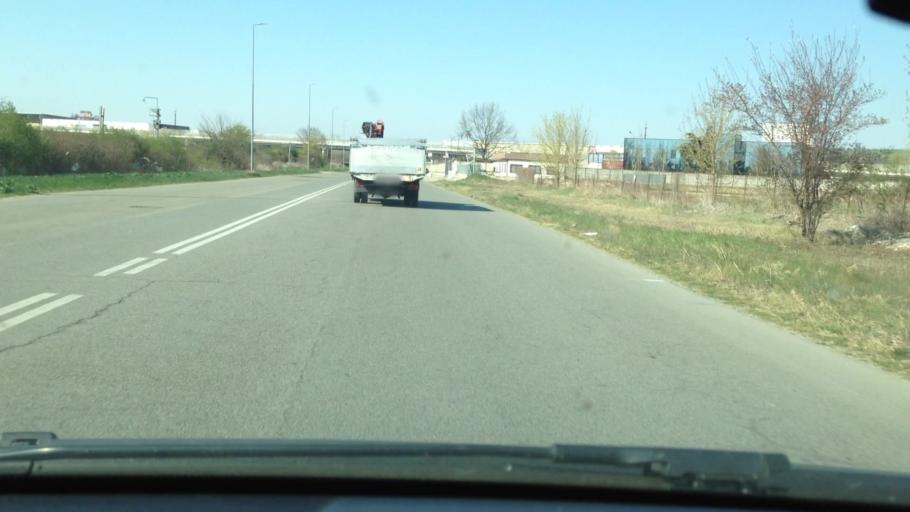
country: IT
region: Piedmont
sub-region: Provincia di Asti
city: Asti
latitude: 44.9091
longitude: 8.2279
